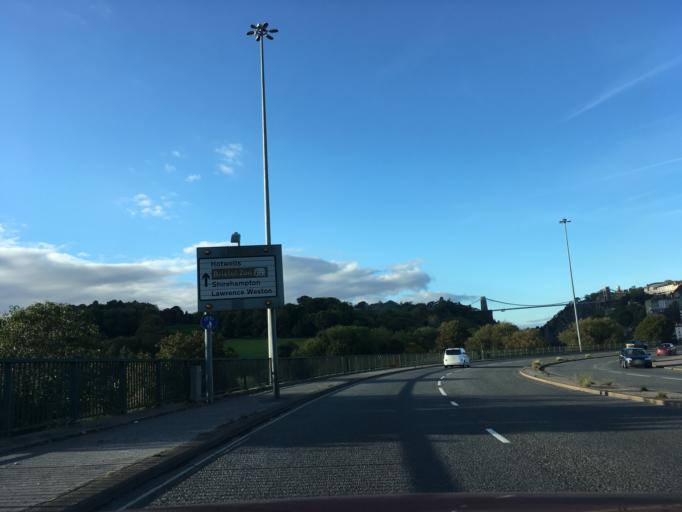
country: GB
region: England
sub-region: Bristol
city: Bristol
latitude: 51.4454
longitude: -2.6239
